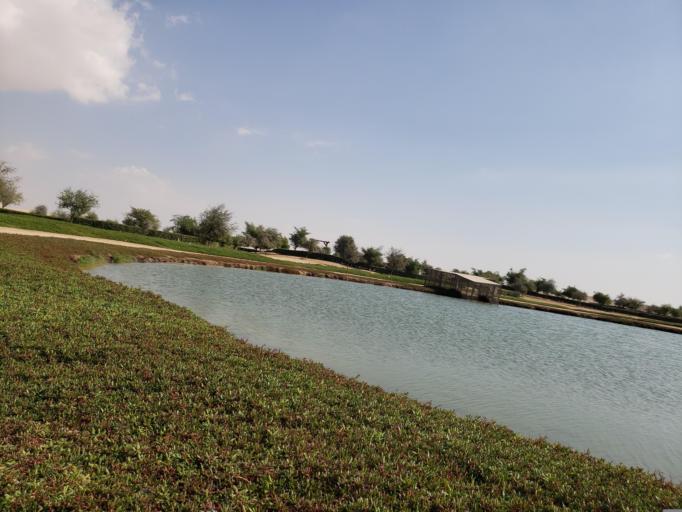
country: AE
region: Dubai
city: Dubai
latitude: 24.8563
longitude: 55.2488
